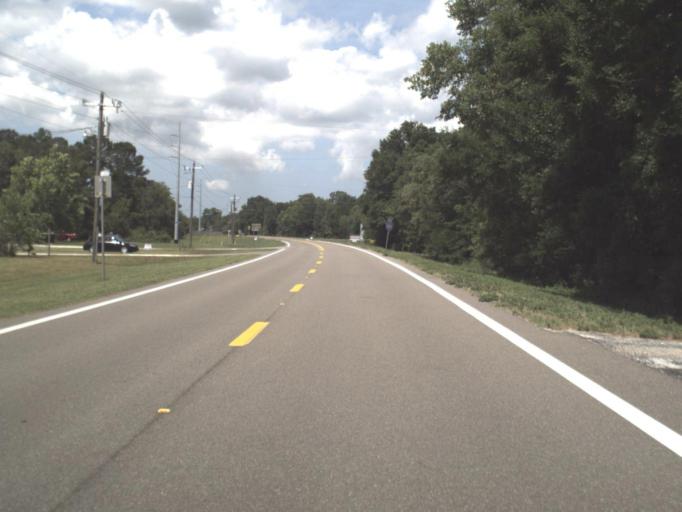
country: US
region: Florida
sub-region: Levy County
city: Chiefland
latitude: 29.2364
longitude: -82.9382
